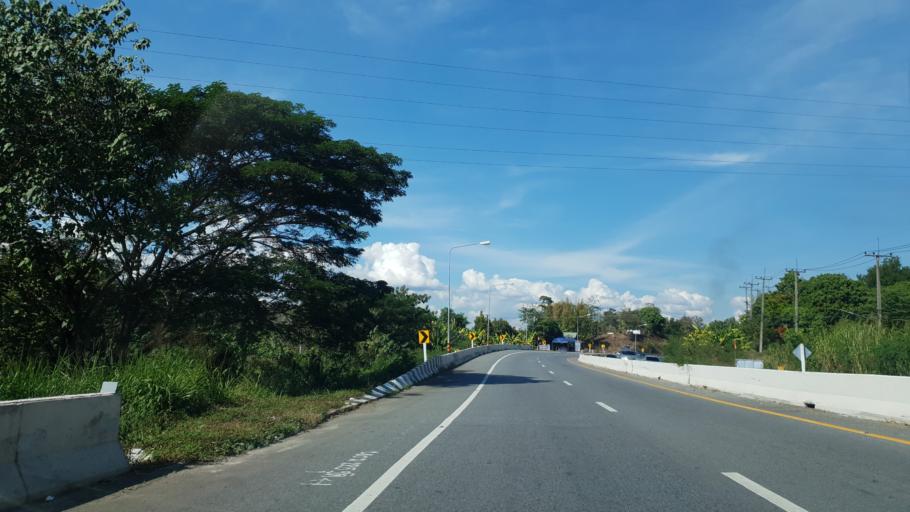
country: TH
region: Phrae
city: Den Chai
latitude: 17.9064
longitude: 100.0655
